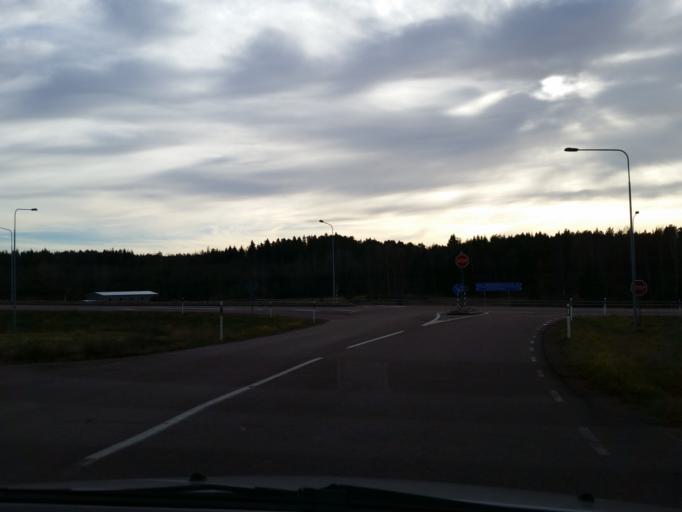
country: AX
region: Alands landsbygd
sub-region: Saltvik
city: Saltvik
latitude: 60.2464
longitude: 20.0412
